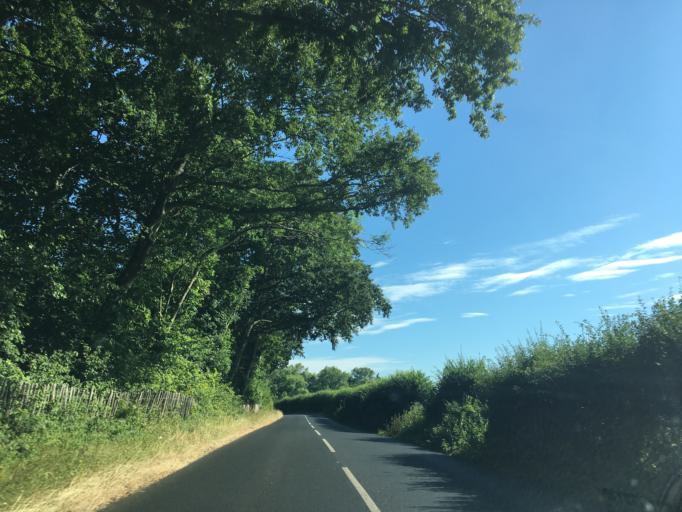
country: GB
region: England
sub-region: Isle of Wight
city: Newport
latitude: 50.6624
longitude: -1.2993
